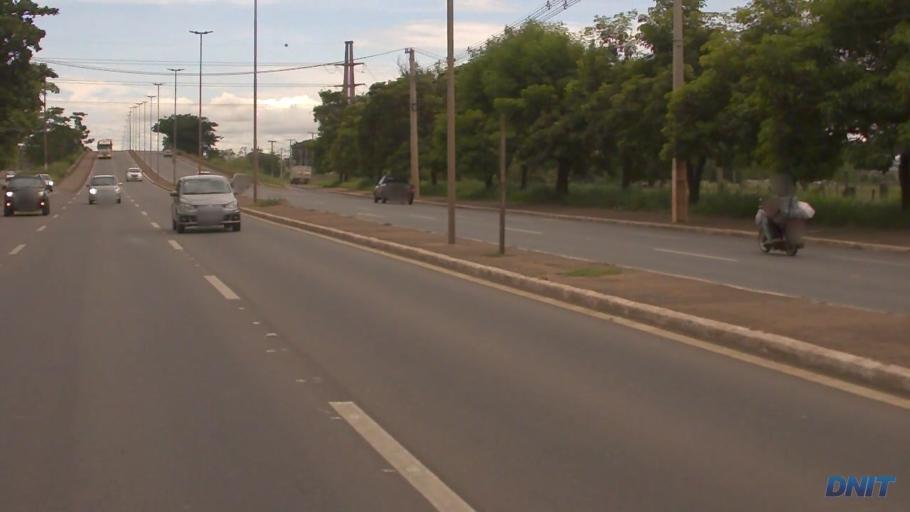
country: BR
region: Mato Grosso
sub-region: Cuiaba
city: Cuiaba
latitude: -15.6479
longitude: -56.0045
